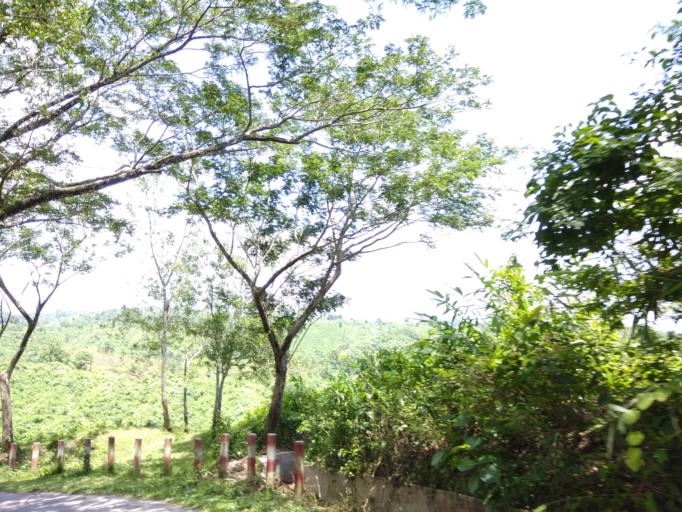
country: BD
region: Chittagong
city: Cox's Bazar
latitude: 21.6647
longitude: 92.3519
